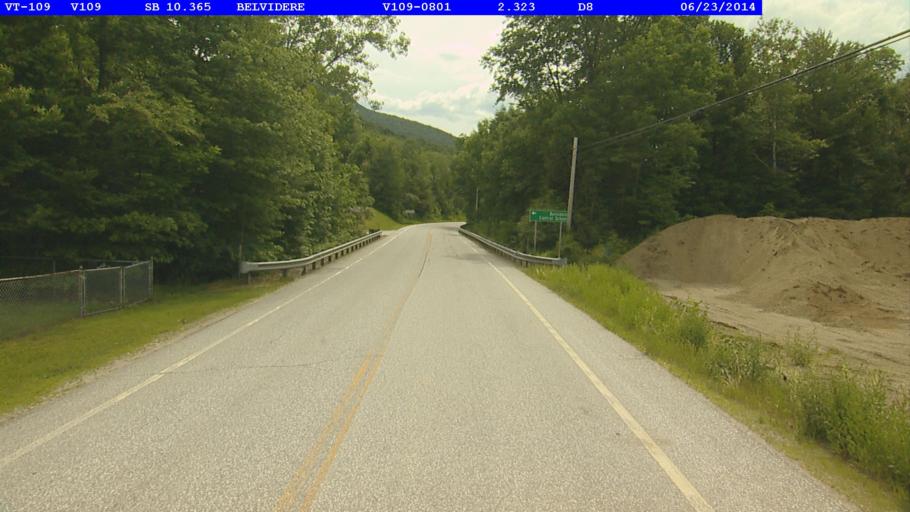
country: US
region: Vermont
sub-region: Lamoille County
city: Johnson
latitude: 44.7481
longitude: -72.7011
